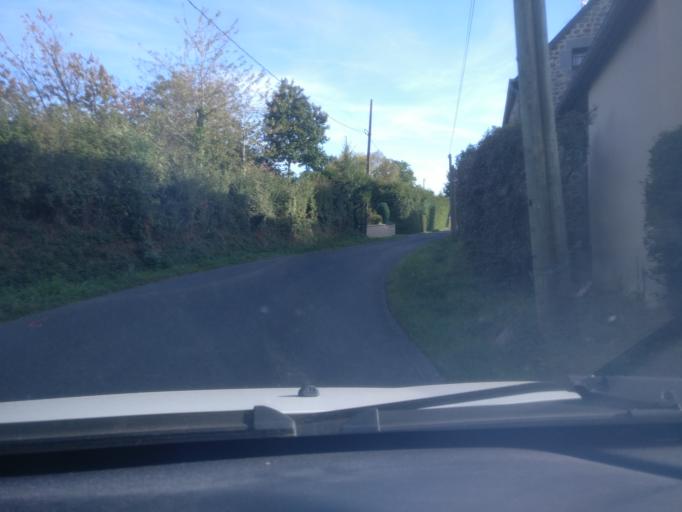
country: FR
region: Lower Normandy
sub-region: Departement de la Manche
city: Marcey-les-Greves
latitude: 48.7018
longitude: -1.3932
